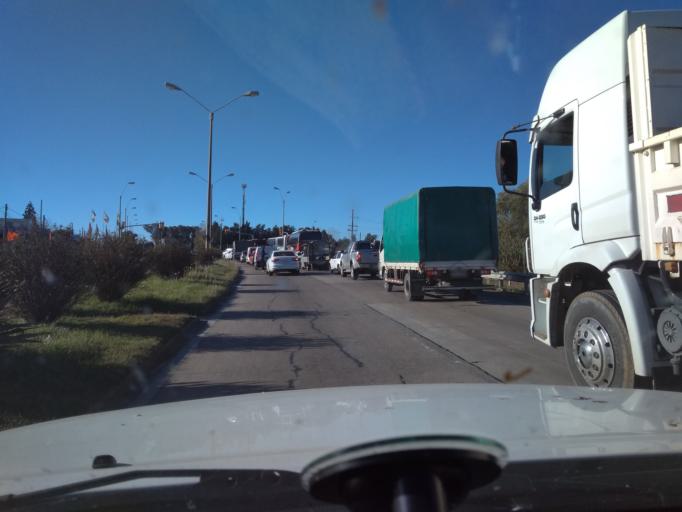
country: UY
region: Canelones
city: Joaquin Suarez
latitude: -34.7712
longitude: -56.0258
